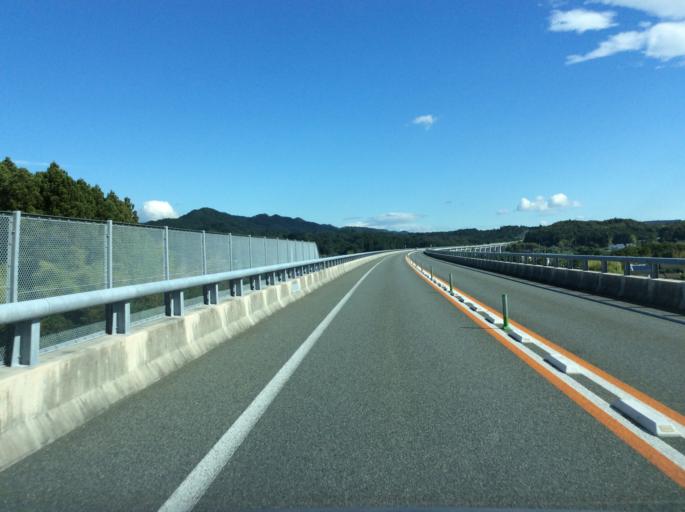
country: JP
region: Fukushima
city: Namie
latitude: 37.2726
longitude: 140.9836
